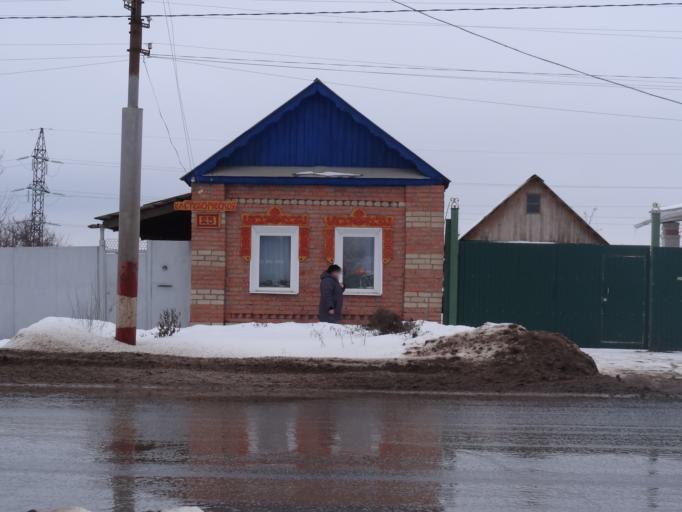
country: RU
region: Saratov
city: Engel's
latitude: 51.4985
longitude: 46.1584
